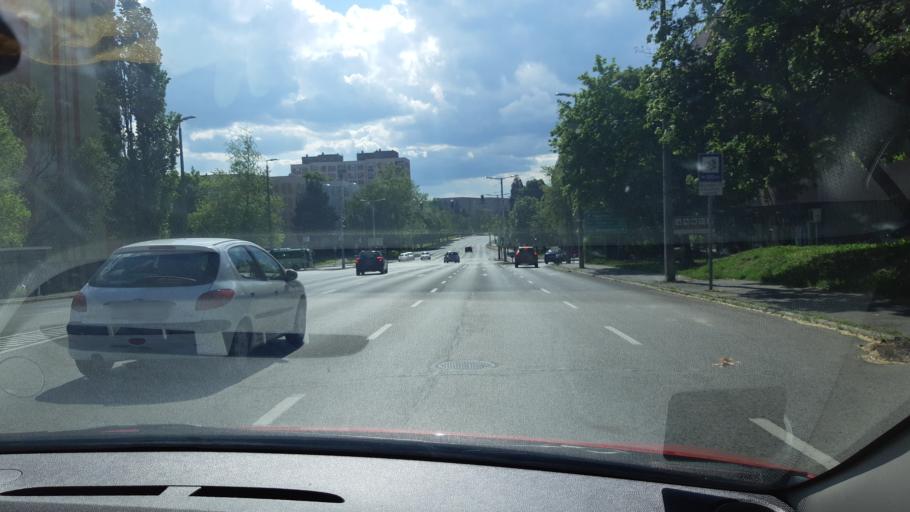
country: HU
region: Somogy
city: Kaposvar
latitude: 46.3642
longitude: 17.7838
